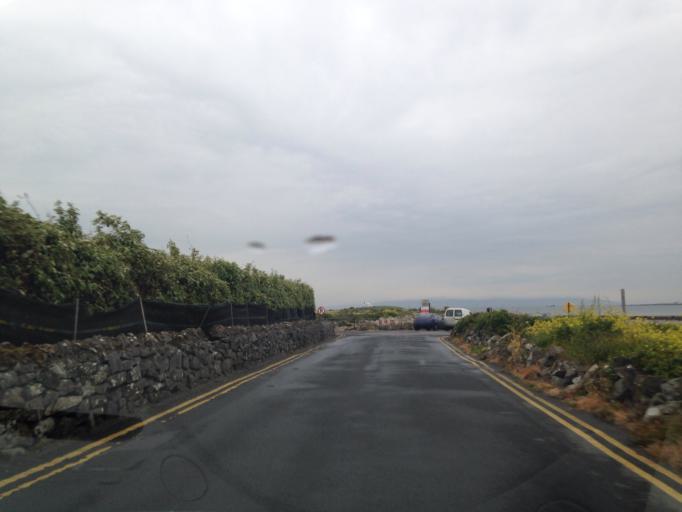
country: IE
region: Connaught
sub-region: County Galway
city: Gaillimh
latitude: 53.2693
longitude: -9.0157
